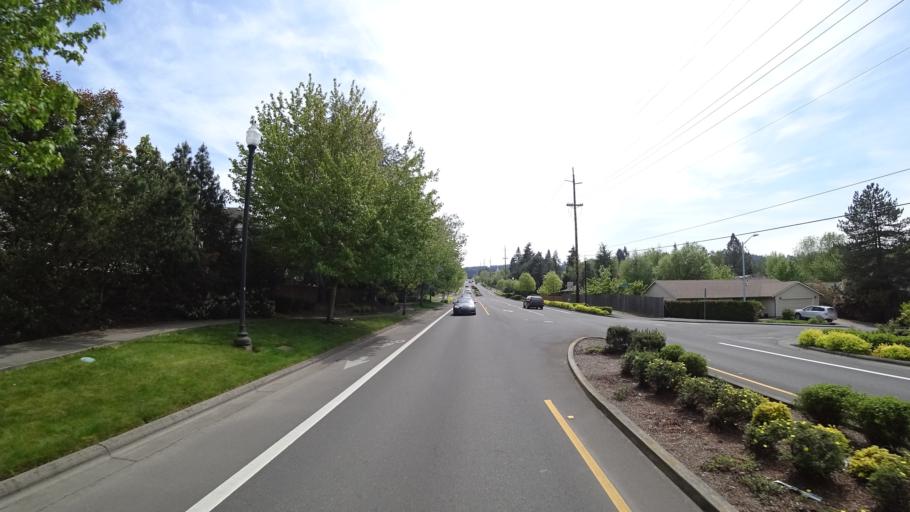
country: US
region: Oregon
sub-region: Washington County
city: Aloha
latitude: 45.4700
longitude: -122.8518
